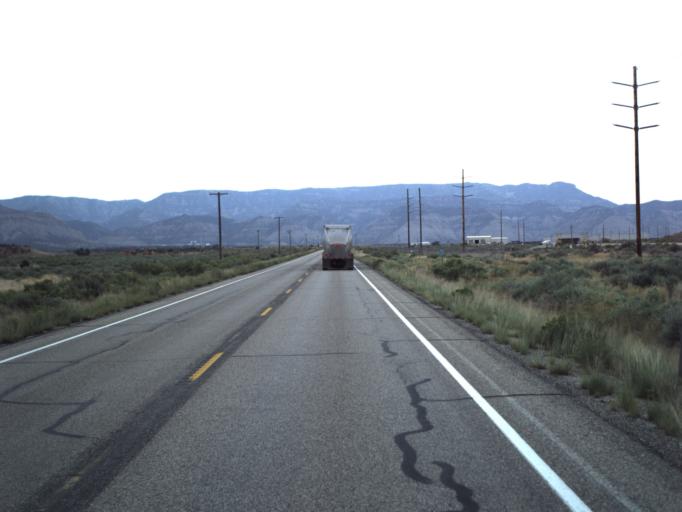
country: US
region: Utah
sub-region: Carbon County
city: East Carbon City
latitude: 39.5356
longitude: -110.4834
